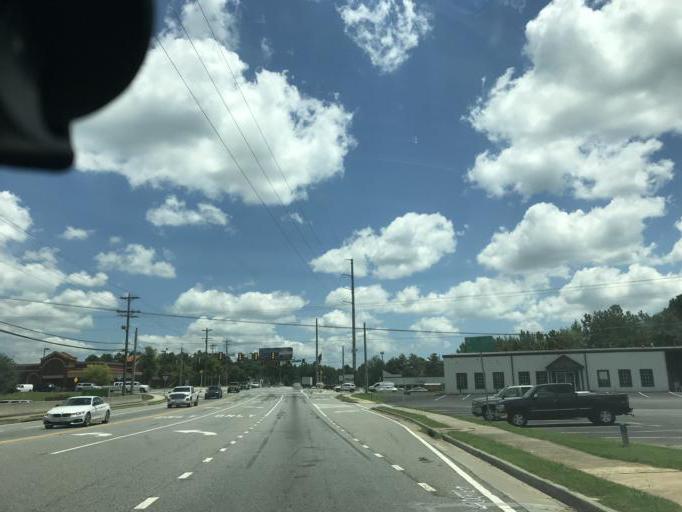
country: US
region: Georgia
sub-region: Fulton County
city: Milton
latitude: 34.1585
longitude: -84.2374
